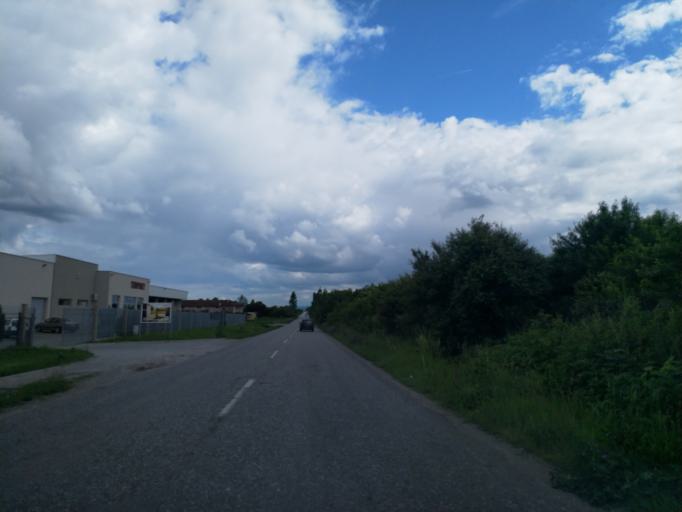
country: RS
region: Central Serbia
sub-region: Pomoravski Okrug
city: Cuprija
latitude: 43.9011
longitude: 21.3796
